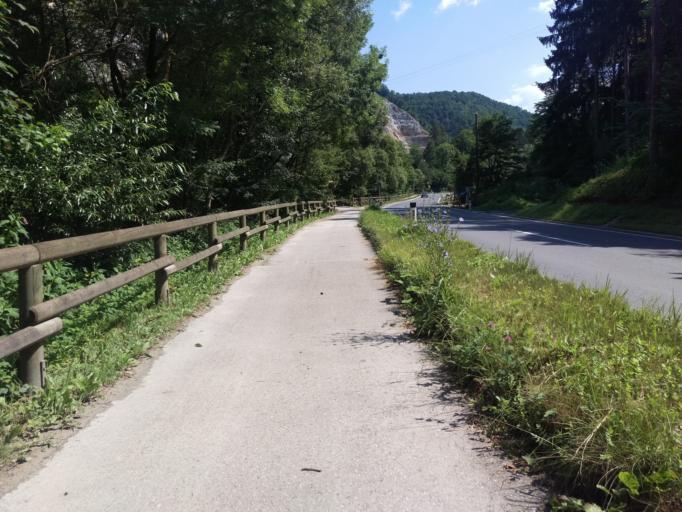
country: AT
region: Styria
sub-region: Politischer Bezirk Graz-Umgebung
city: Stattegg
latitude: 47.1312
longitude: 15.4499
